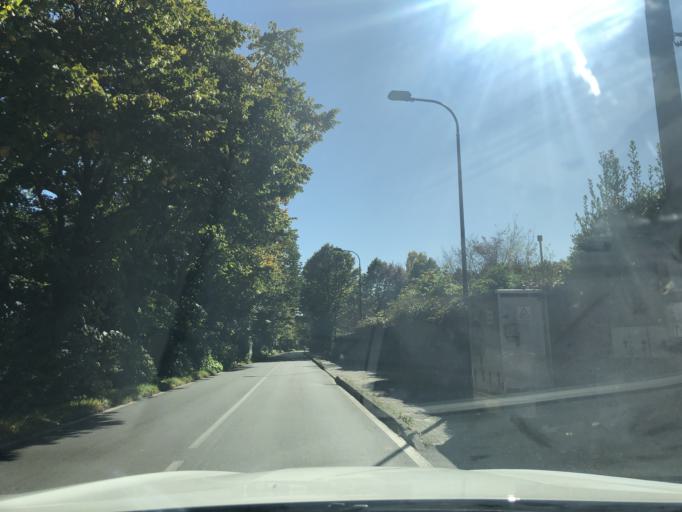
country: IT
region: Lombardy
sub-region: Provincia di Monza e Brianza
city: Villaggio del Sole
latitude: 45.6239
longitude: 9.1191
